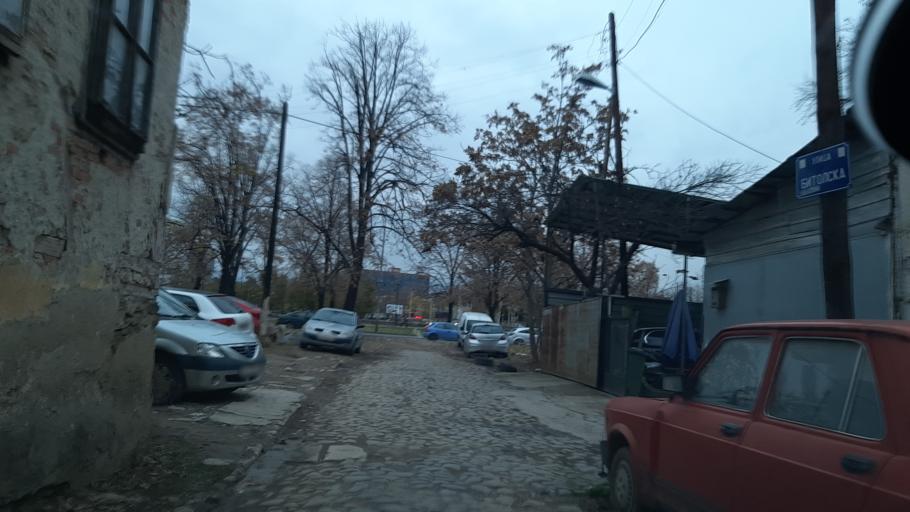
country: MK
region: Karpos
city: Skopje
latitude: 41.9937
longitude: 21.4401
